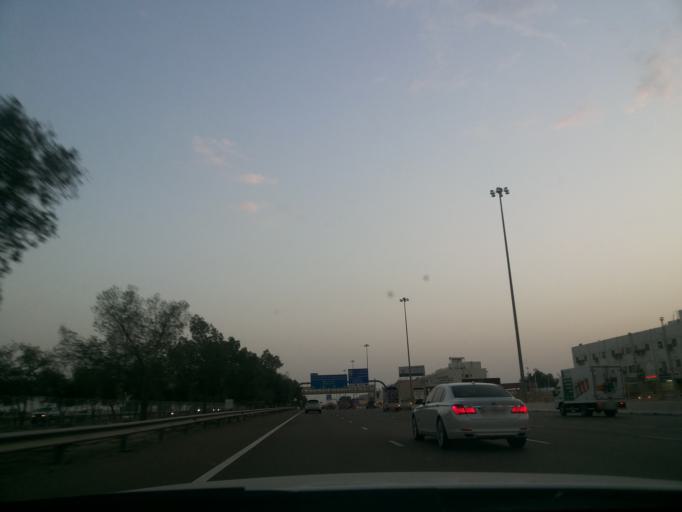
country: AE
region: Abu Dhabi
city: Abu Dhabi
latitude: 24.5581
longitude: 54.6951
